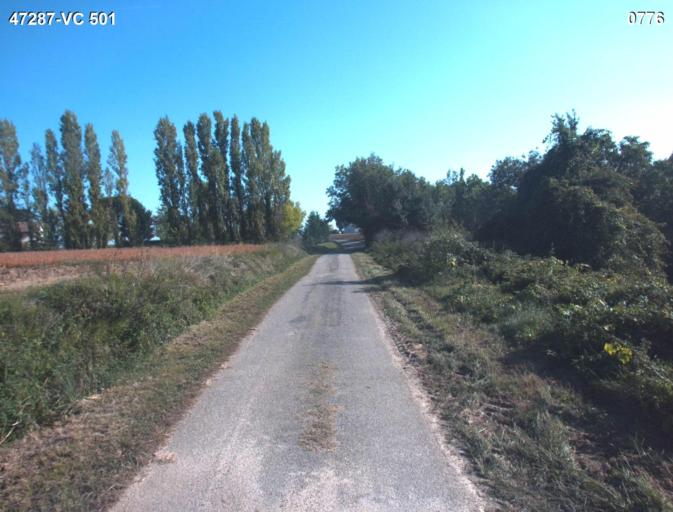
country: FR
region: Aquitaine
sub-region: Departement du Lot-et-Garonne
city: Laplume
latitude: 44.1136
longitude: 0.4606
